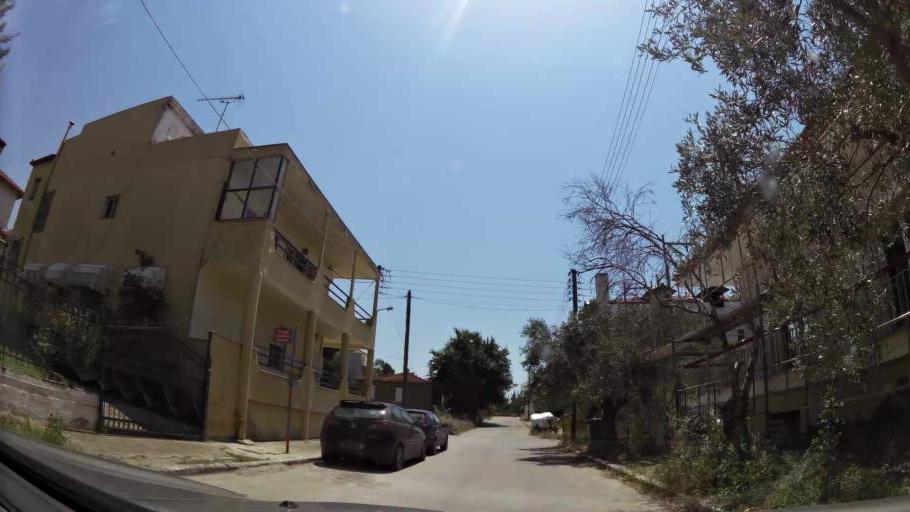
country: GR
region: Central Macedonia
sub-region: Nomos Thessalonikis
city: Nea Michaniona
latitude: 40.4759
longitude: 22.8708
